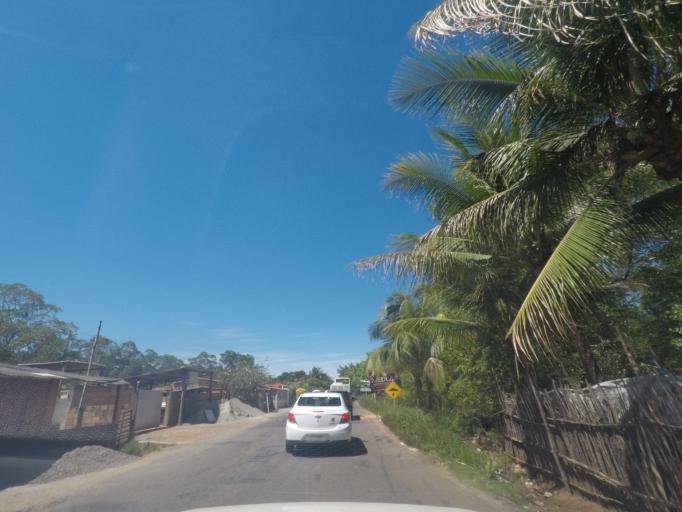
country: BR
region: Bahia
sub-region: Taperoa
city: Taperoa
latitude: -13.4802
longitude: -39.0904
